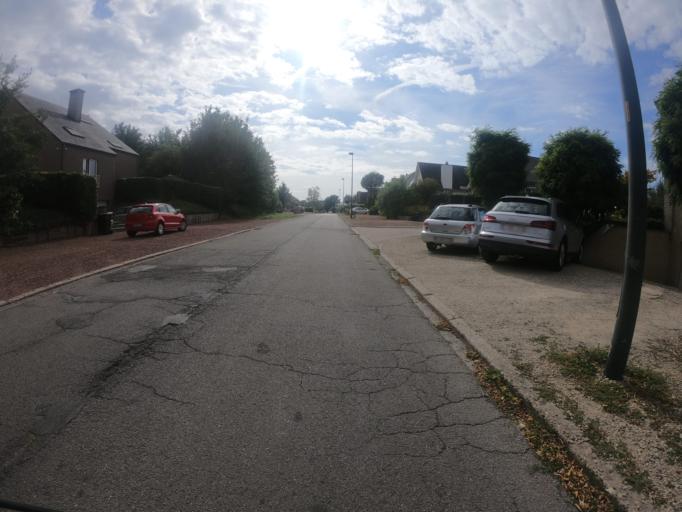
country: BE
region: Flanders
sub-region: Provincie Vlaams-Brabant
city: Wezembeek-Oppem
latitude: 50.8444
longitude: 4.5096
